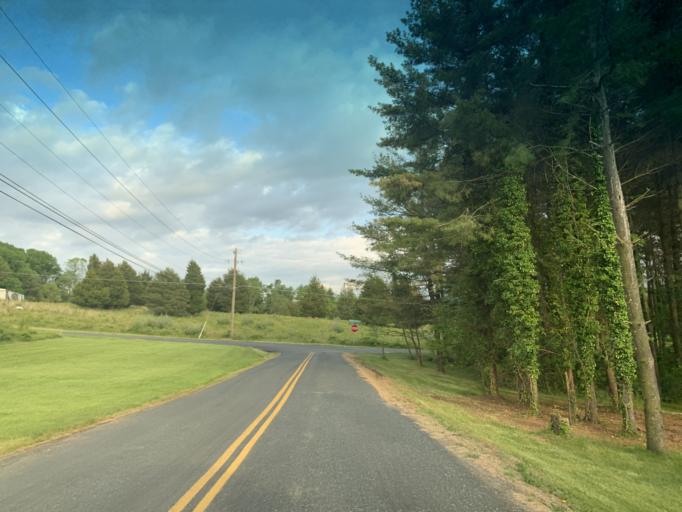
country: US
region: Pennsylvania
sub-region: York County
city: Susquehanna Trails
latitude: 39.6711
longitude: -76.2309
